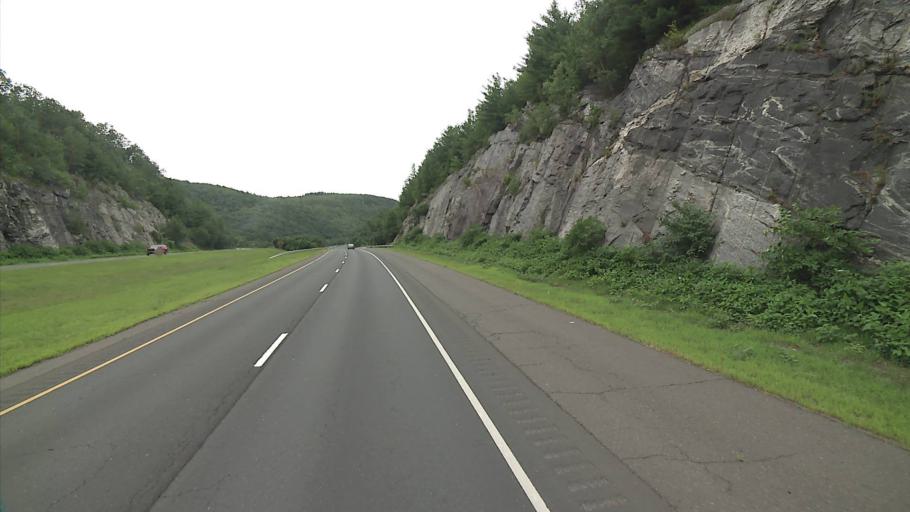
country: US
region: Connecticut
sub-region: New Haven County
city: Seymour
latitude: 41.4416
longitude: -73.0666
